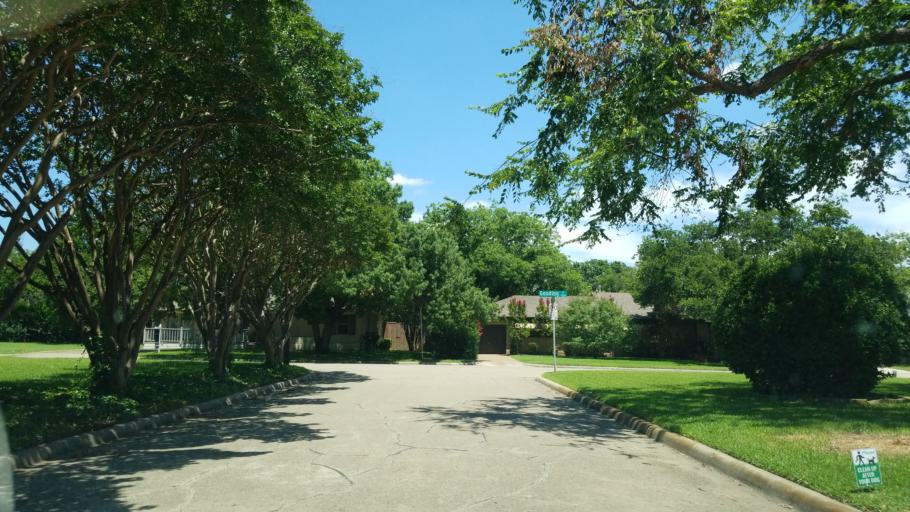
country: US
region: Texas
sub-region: Dallas County
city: University Park
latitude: 32.8788
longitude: -96.8442
